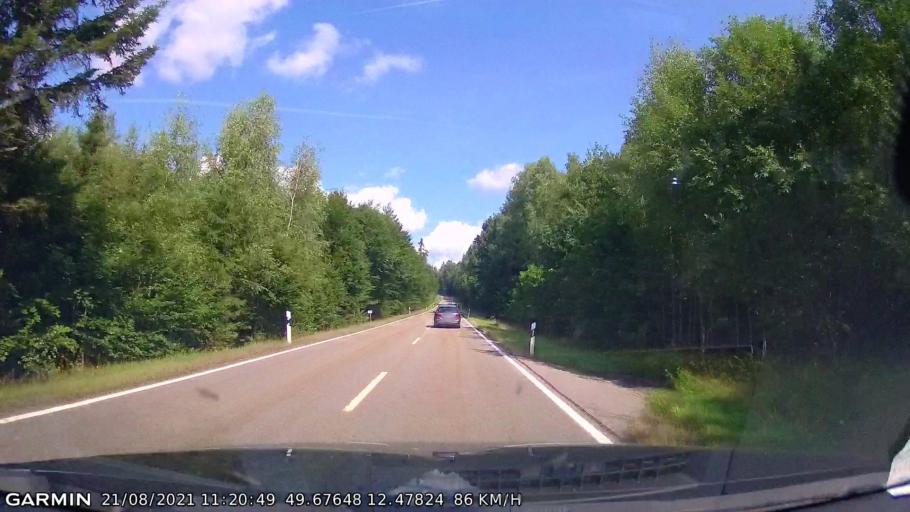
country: DE
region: Bavaria
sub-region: Upper Palatinate
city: Waidhaus
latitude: 49.6766
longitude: 12.4782
